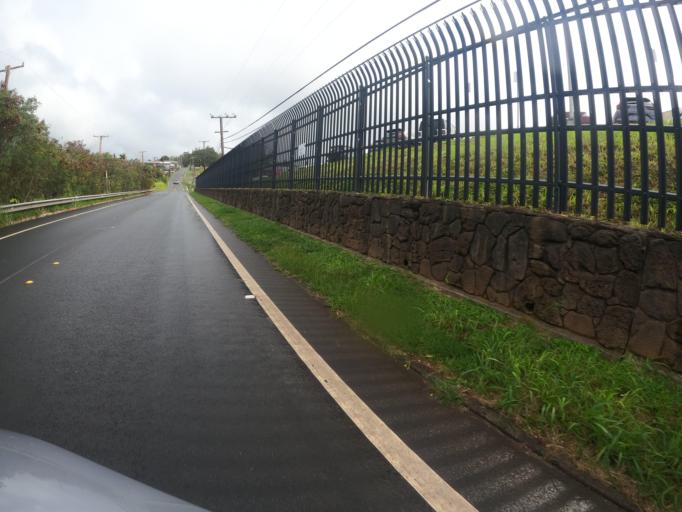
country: US
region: Hawaii
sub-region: Honolulu County
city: Halawa Heights
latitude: 21.3878
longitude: -157.9088
